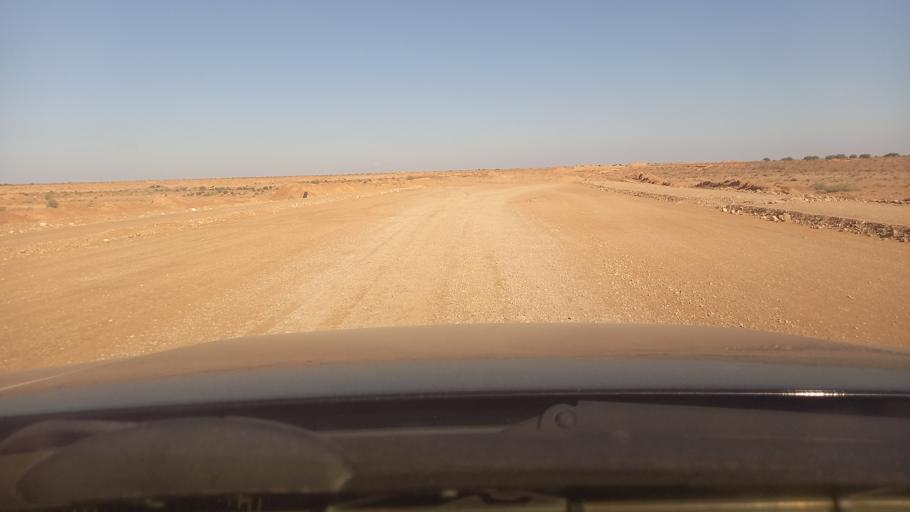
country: TN
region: Madanin
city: Medenine
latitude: 33.1455
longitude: 10.5064
